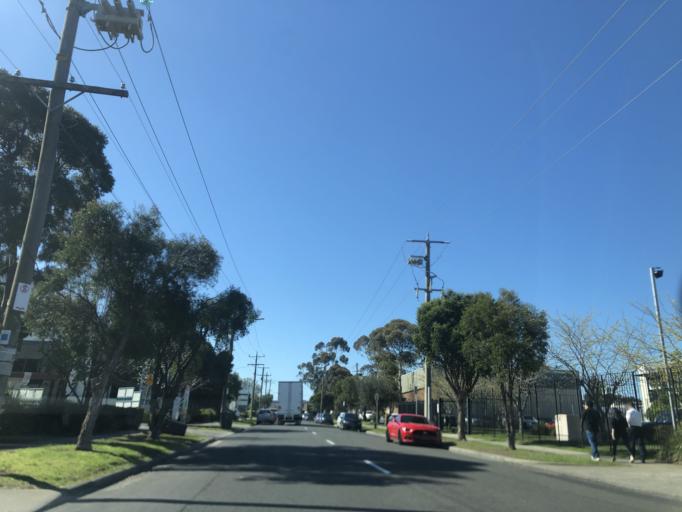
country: AU
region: Victoria
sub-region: Monash
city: Notting Hill
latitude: -37.9026
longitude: 145.1379
